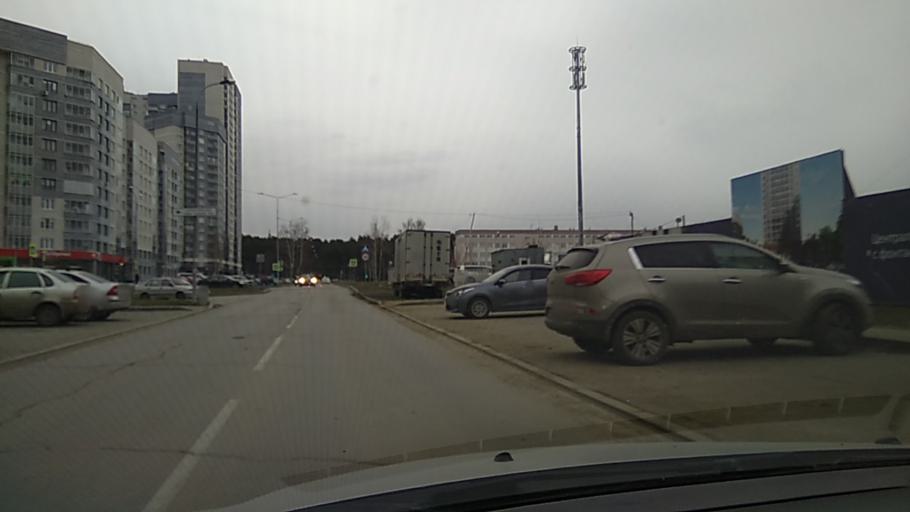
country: RU
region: Sverdlovsk
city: Sovkhoznyy
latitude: 56.7802
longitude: 60.5510
